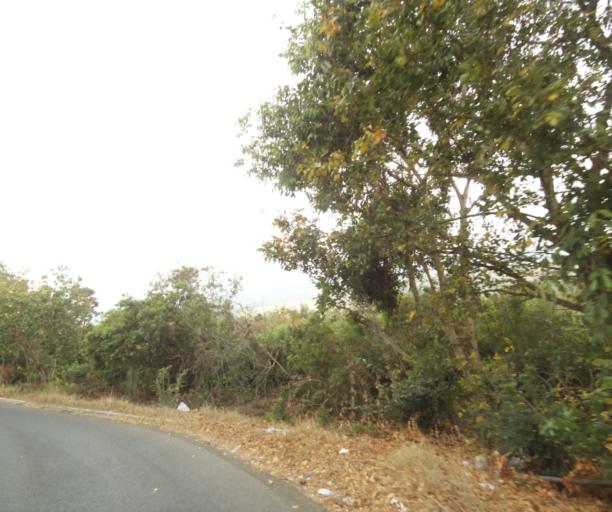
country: RE
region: Reunion
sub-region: Reunion
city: Saint-Paul
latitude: -20.9893
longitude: 55.2927
